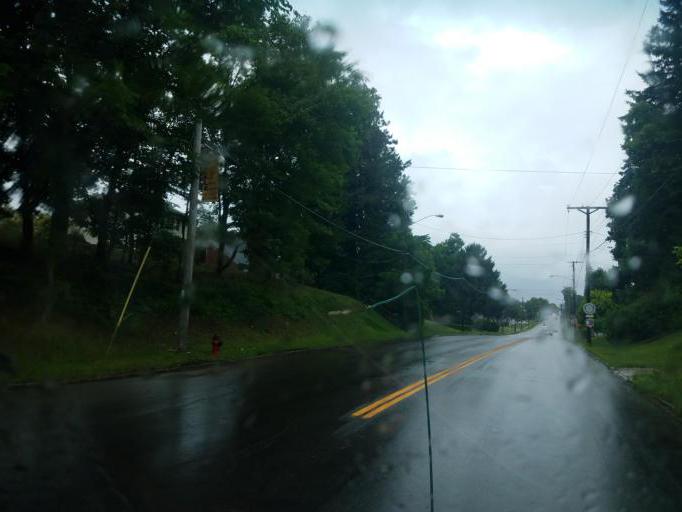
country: US
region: Ohio
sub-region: Stark County
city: Canton
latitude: 40.7914
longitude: -81.3395
